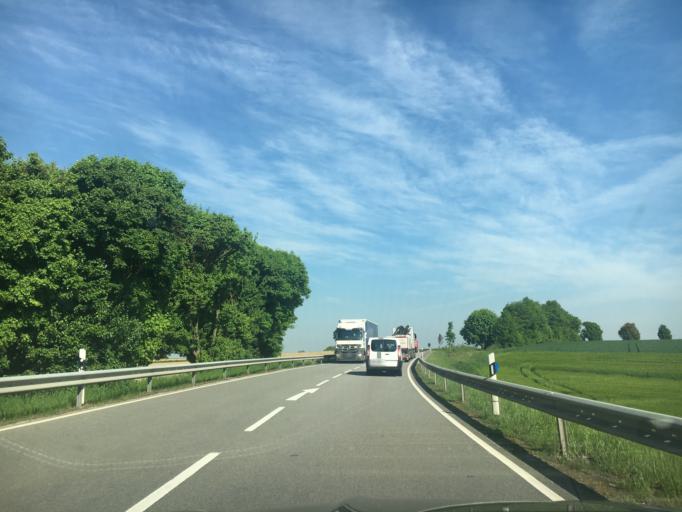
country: DE
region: Bavaria
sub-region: Upper Bavaria
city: Neumarkt-Sankt Veit
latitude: 48.3429
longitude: 12.5109
